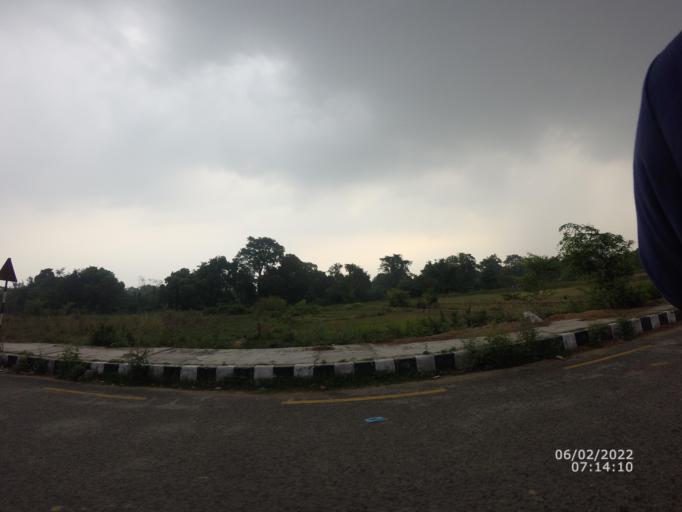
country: NP
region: Western Region
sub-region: Lumbini Zone
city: Bhairahawa
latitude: 27.4798
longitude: 83.4442
